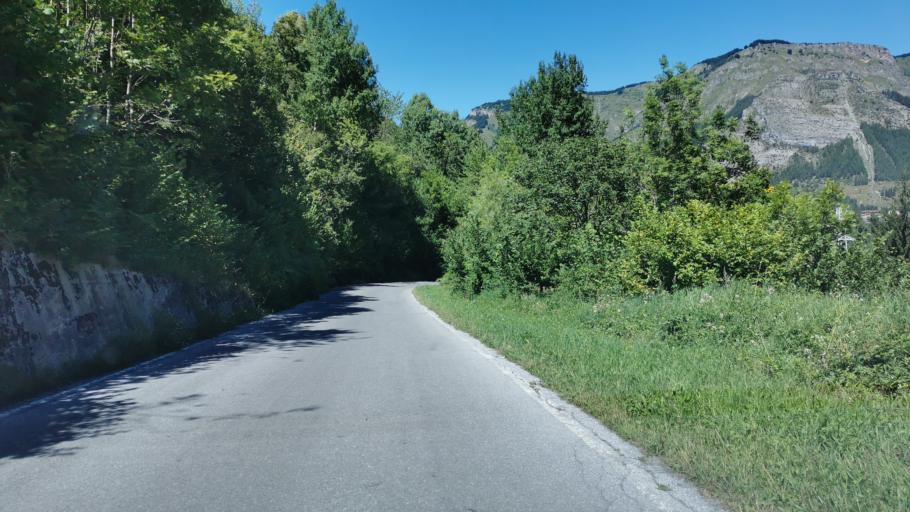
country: IT
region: Piedmont
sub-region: Provincia di Cuneo
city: Entracque
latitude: 44.2285
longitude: 7.3885
